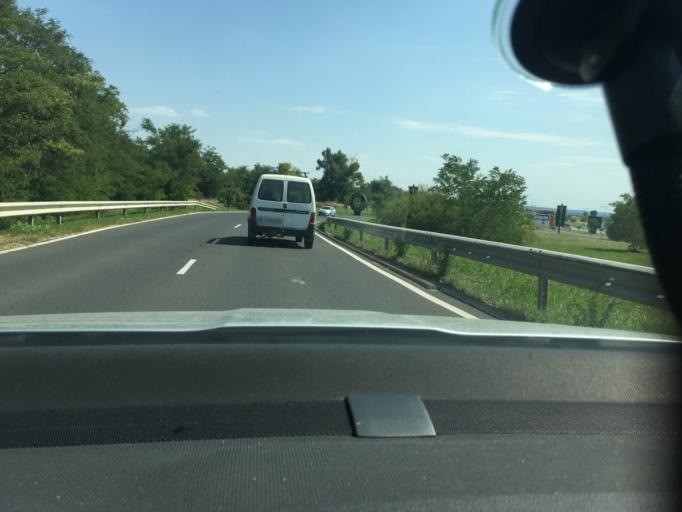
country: HU
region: Pest
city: Ecser
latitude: 47.4631
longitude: 19.3347
